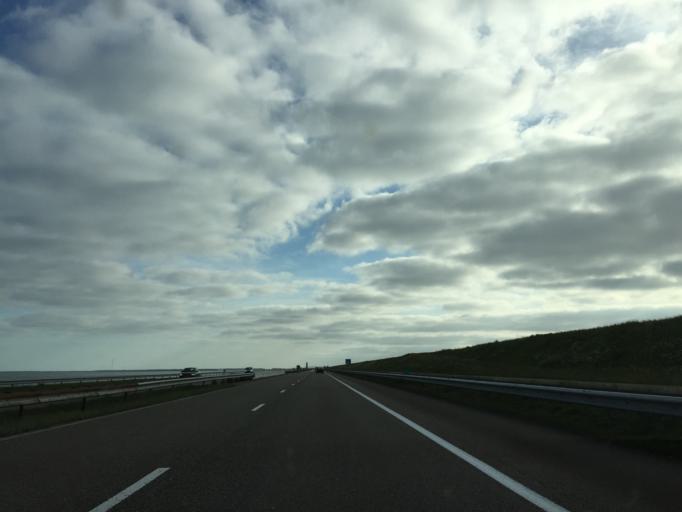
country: NL
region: North Holland
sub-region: Gemeente Hollands Kroon
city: Den Oever
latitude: 52.9781
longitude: 5.1256
